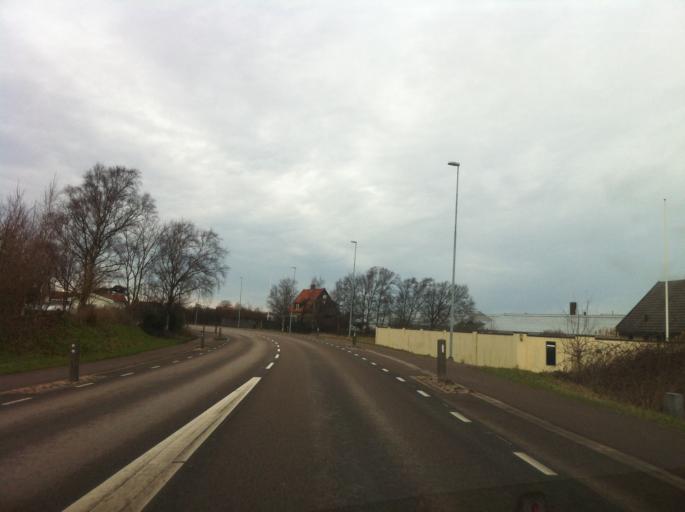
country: SE
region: Skane
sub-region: Hoganas Kommun
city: Hoganas
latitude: 56.1413
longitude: 12.5868
